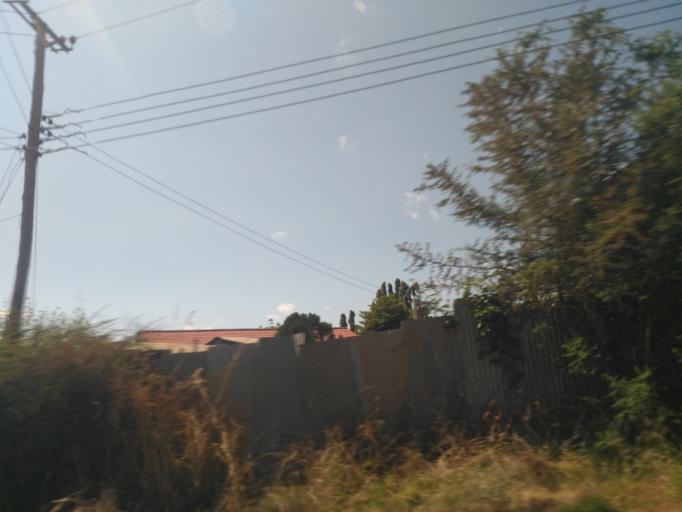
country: TZ
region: Dodoma
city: Dodoma
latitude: -6.1644
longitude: 35.7609
